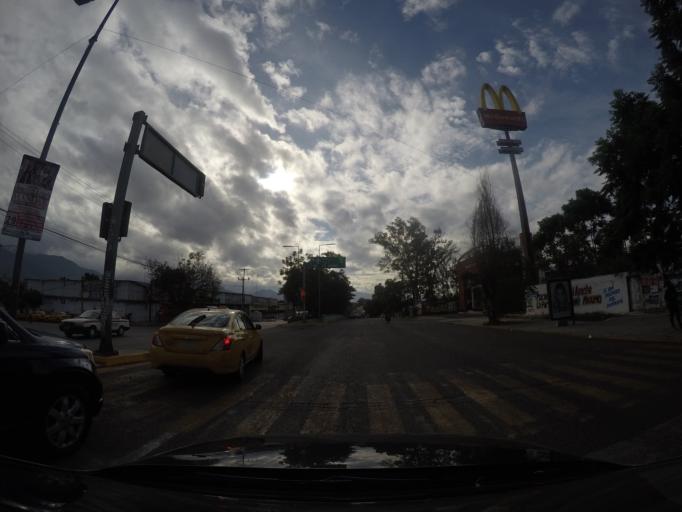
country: MX
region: Oaxaca
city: Oaxaca de Juarez
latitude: 17.0702
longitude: -96.7117
